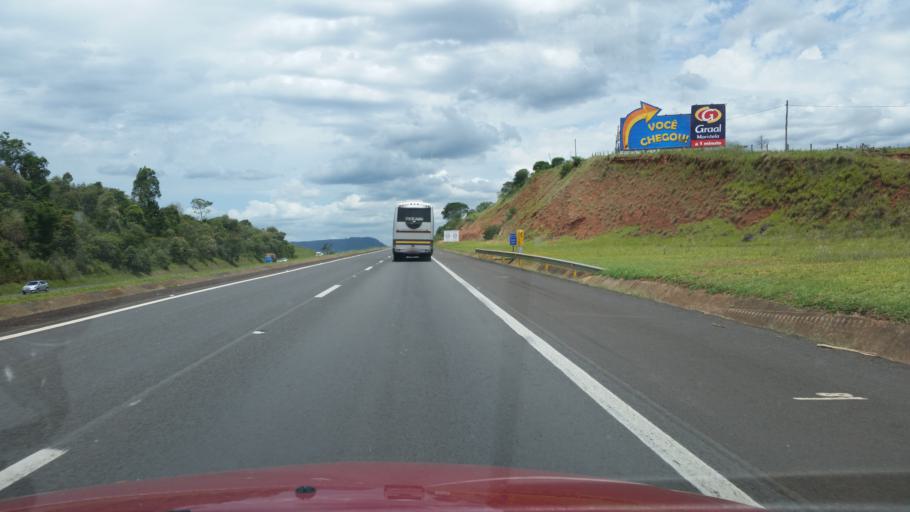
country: BR
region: Sao Paulo
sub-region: Itatinga
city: Itatinga
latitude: -23.1356
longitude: -48.4548
